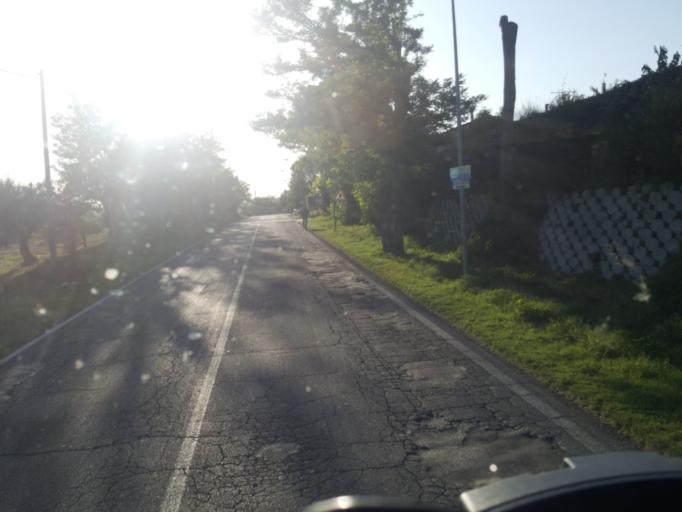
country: IT
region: Latium
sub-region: Citta metropolitana di Roma Capitale
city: Bivio di Capanelle
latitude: 42.1239
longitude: 12.5817
